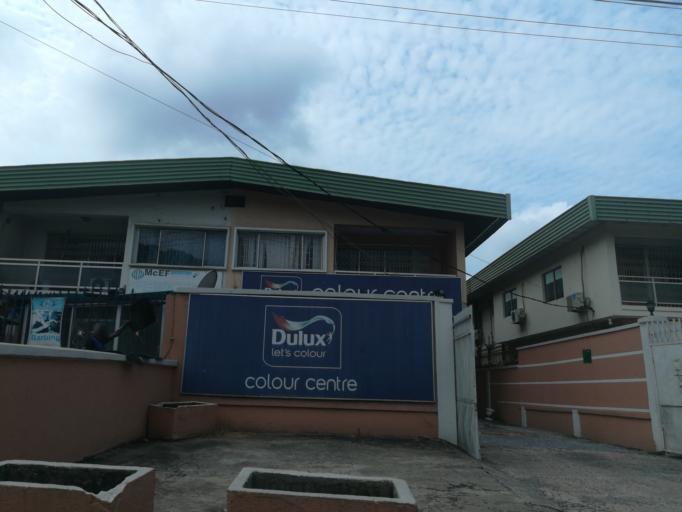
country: NG
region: Lagos
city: Somolu
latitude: 6.5472
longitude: 3.3838
